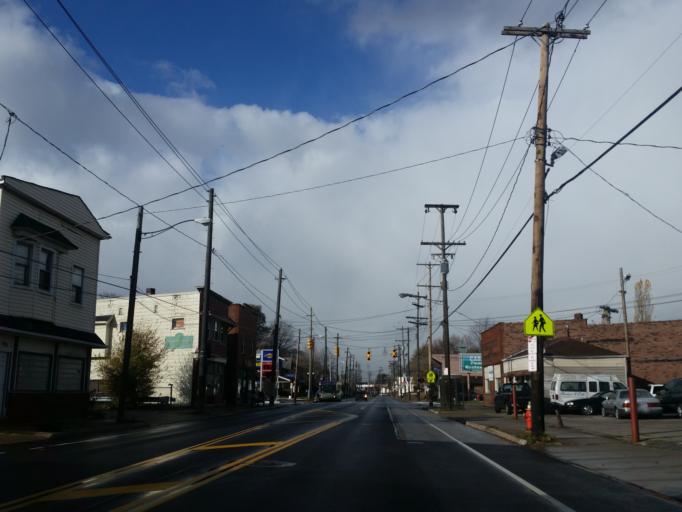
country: US
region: Ohio
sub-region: Cuyahoga County
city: Brooklyn Heights
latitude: 41.4351
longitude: -81.6972
